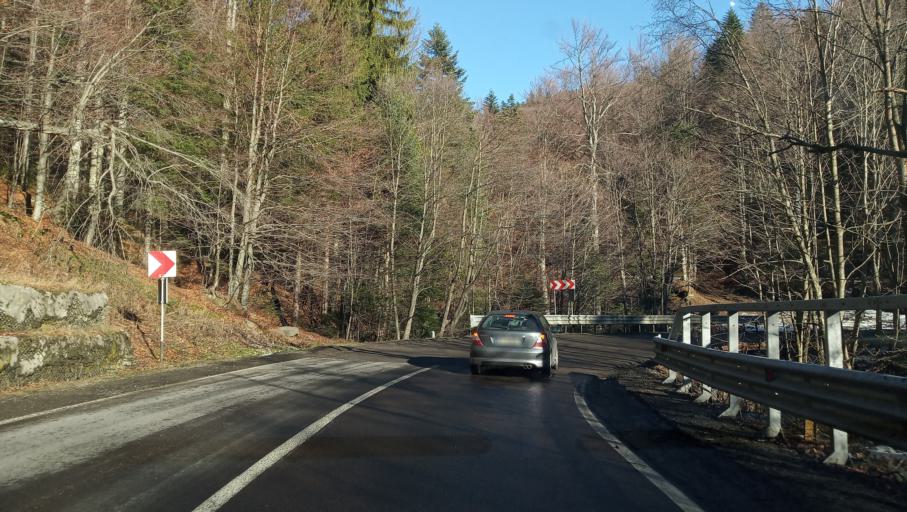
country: RO
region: Brasov
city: Crivina
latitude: 45.4731
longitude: 25.9328
